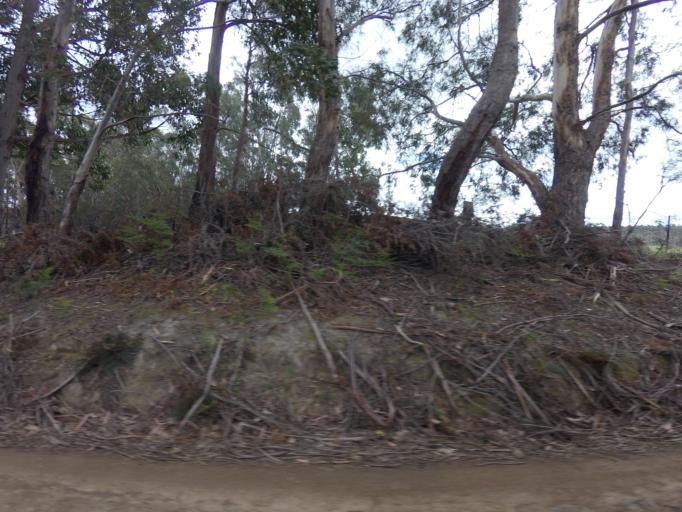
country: AU
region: Tasmania
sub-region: Huon Valley
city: Geeveston
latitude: -43.4266
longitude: 146.9965
